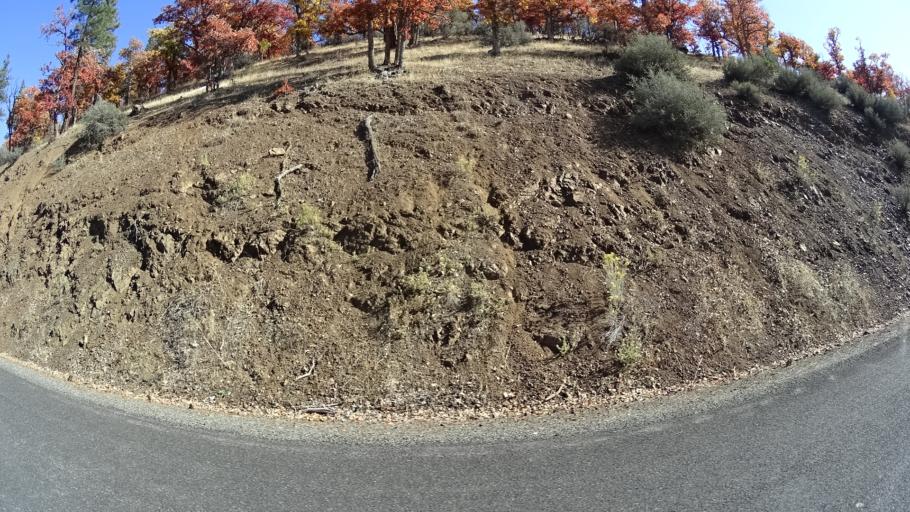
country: US
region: California
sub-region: Siskiyou County
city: Yreka
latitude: 41.6670
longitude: -122.8502
